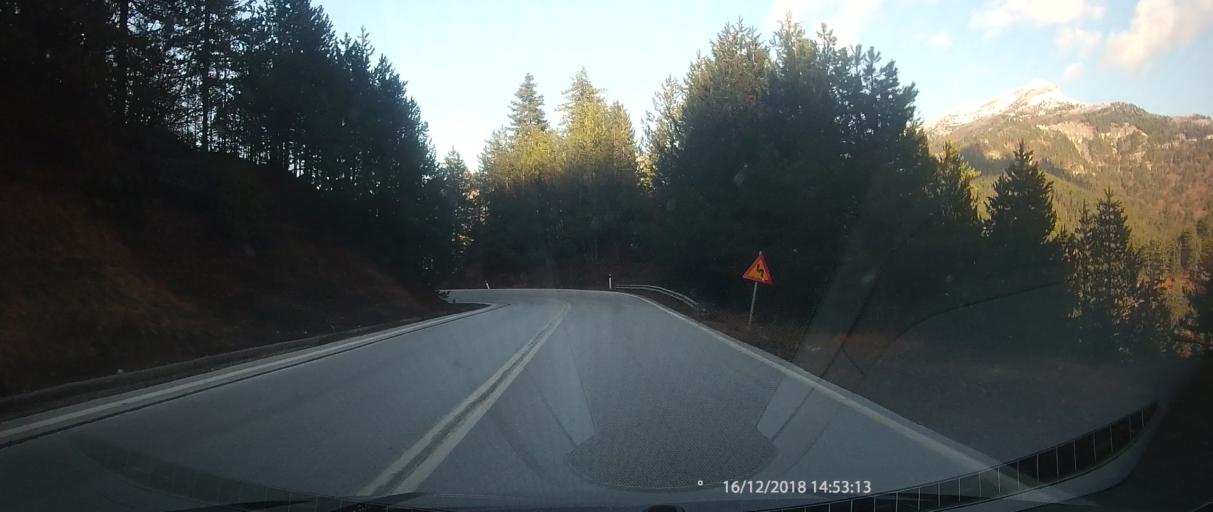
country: GR
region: West Macedonia
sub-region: Nomos Kastorias
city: Nestorio
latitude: 40.2083
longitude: 21.0583
